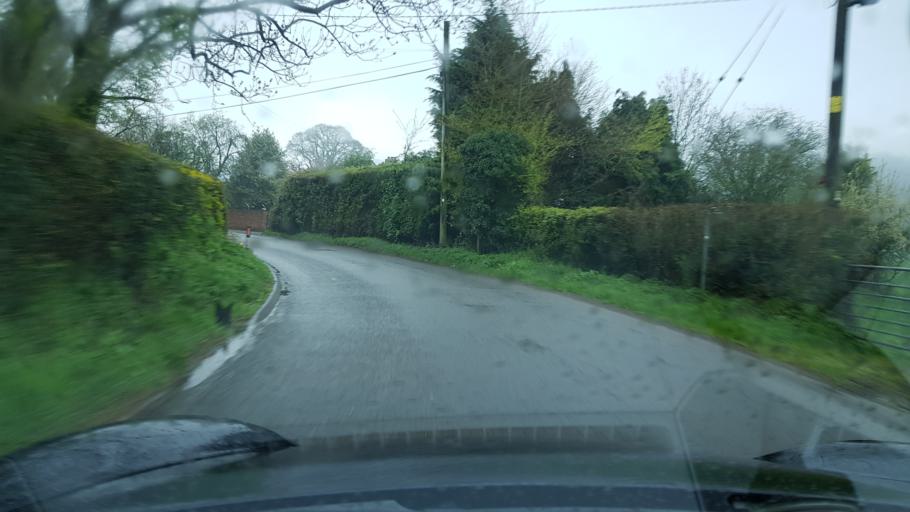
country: GB
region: England
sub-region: Gloucestershire
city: Mitcheldean
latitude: 51.8746
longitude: -2.4869
